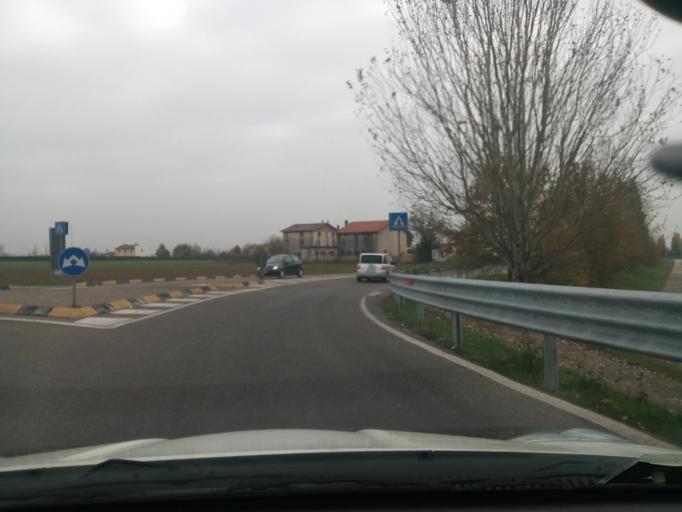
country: IT
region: Veneto
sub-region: Provincia di Vicenza
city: Thiene
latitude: 45.6927
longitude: 11.4651
